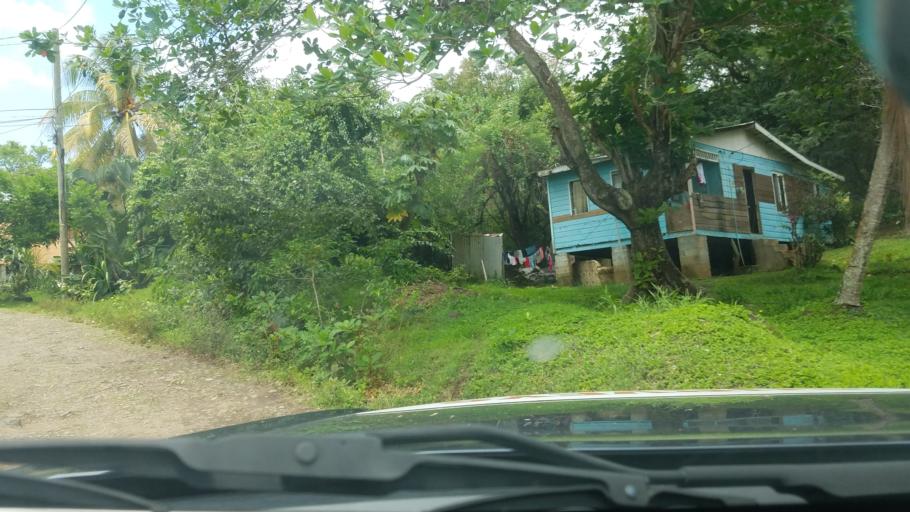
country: LC
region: Gros-Islet
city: Gros Islet
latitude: 14.0522
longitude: -60.9289
